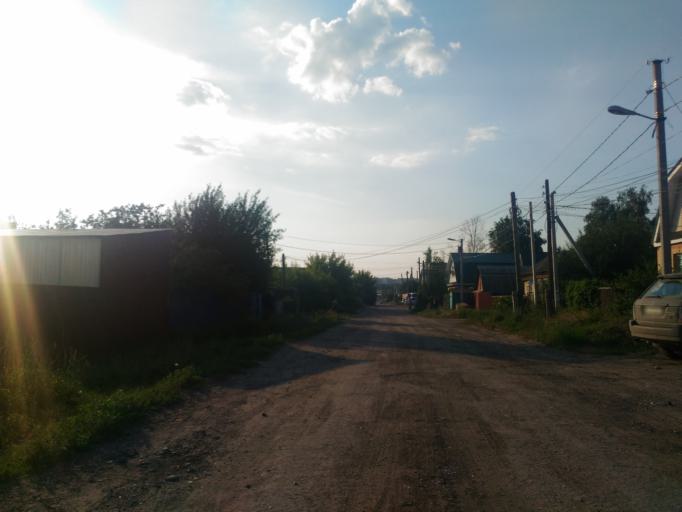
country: RU
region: Ulyanovsk
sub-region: Ulyanovskiy Rayon
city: Ulyanovsk
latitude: 54.3374
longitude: 48.3648
